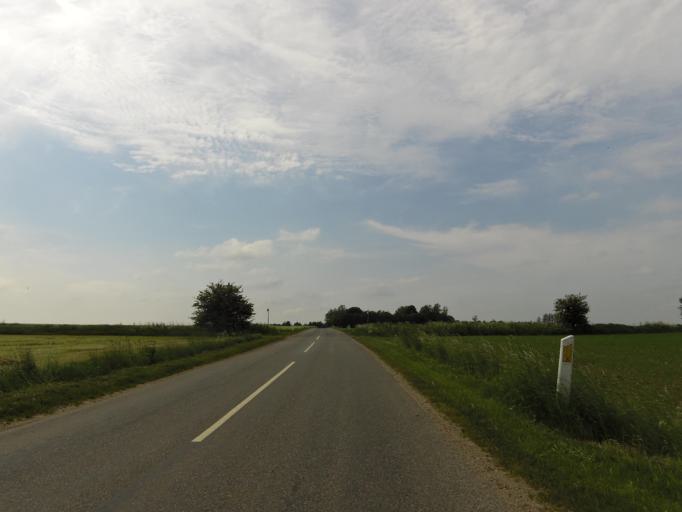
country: DK
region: South Denmark
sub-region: Haderslev Kommune
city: Gram
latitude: 55.2772
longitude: 9.1104
